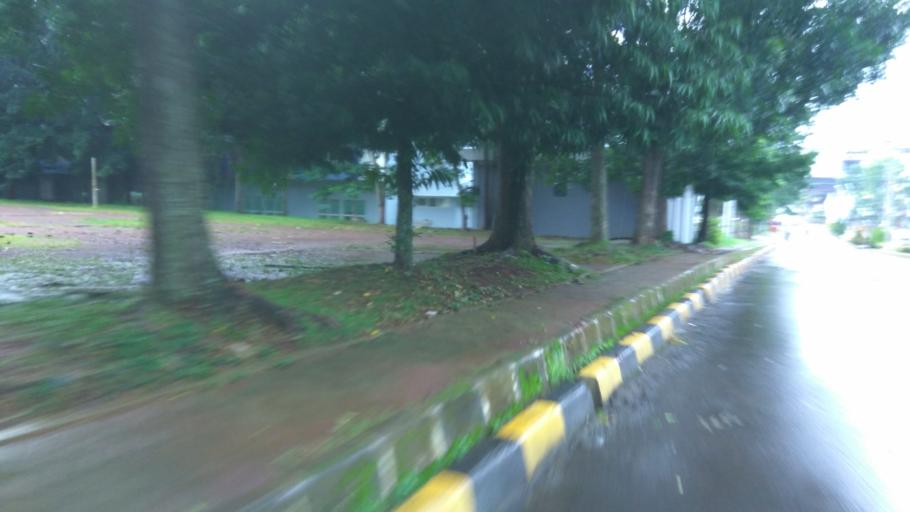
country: ID
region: Central Java
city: Semarang
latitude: -7.0488
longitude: 110.3967
